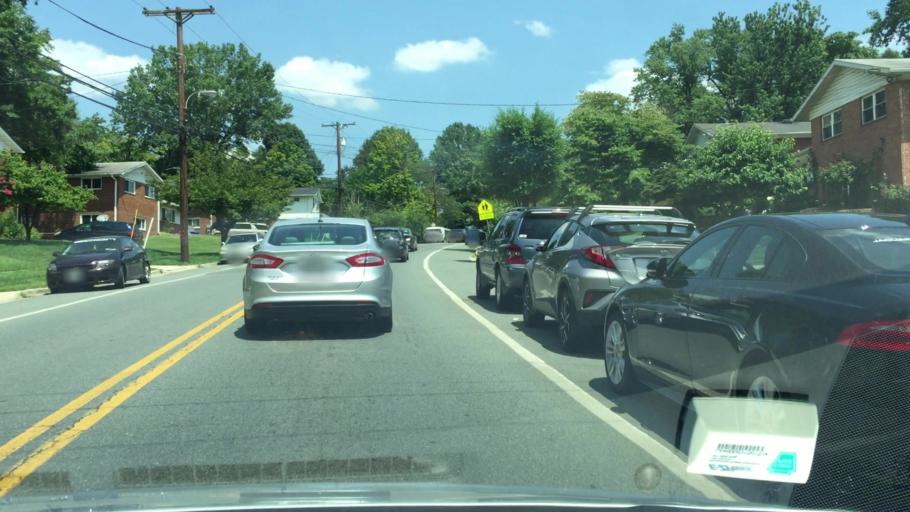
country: US
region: Maryland
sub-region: Montgomery County
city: North Bethesda
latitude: 39.0705
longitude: -77.1033
